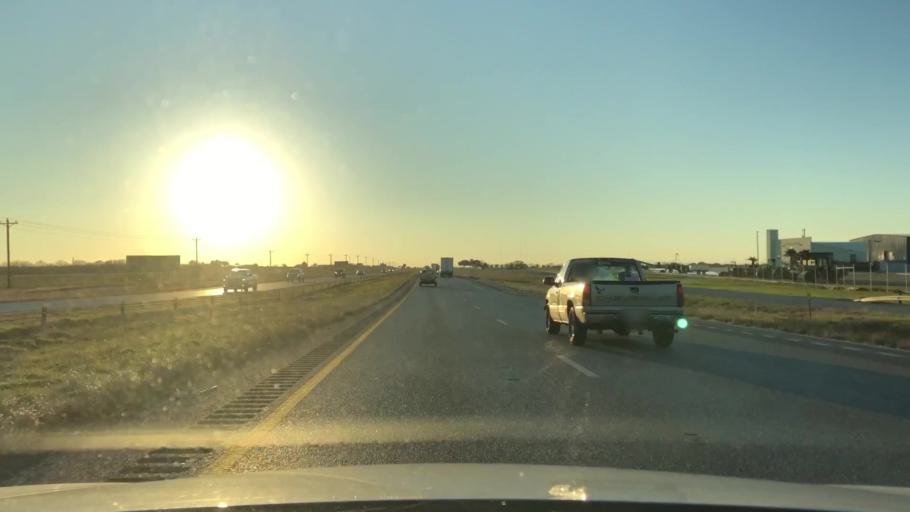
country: US
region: Texas
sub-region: Guadalupe County
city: Marion
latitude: 29.5346
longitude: -98.0921
